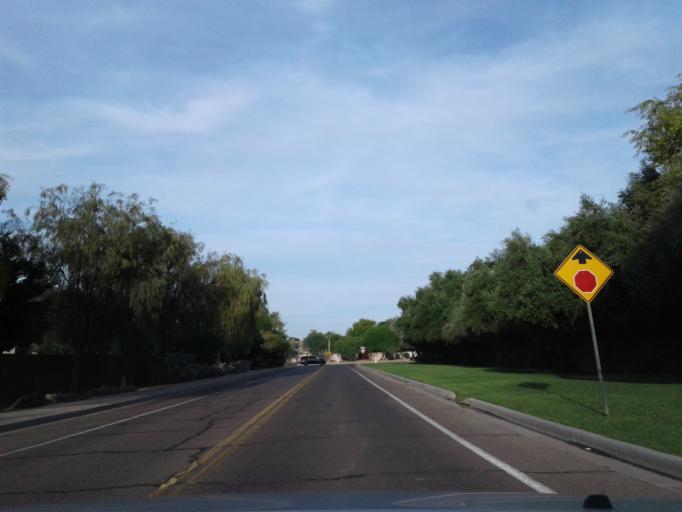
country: US
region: Arizona
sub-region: Maricopa County
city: Paradise Valley
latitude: 33.5585
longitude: -111.9452
